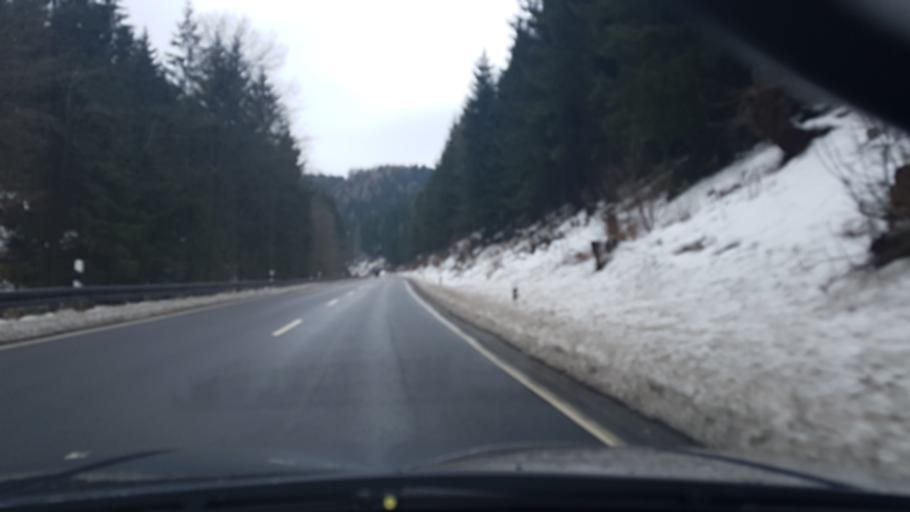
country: DE
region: Lower Saxony
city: Goslar
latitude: 51.8768
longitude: 10.3993
